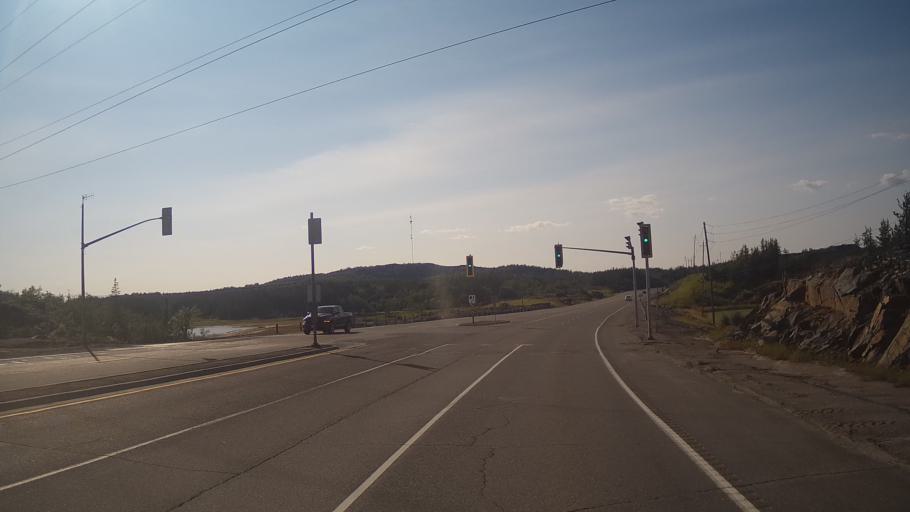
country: CA
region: Ontario
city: Greater Sudbury
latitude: 46.5051
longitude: -81.0462
